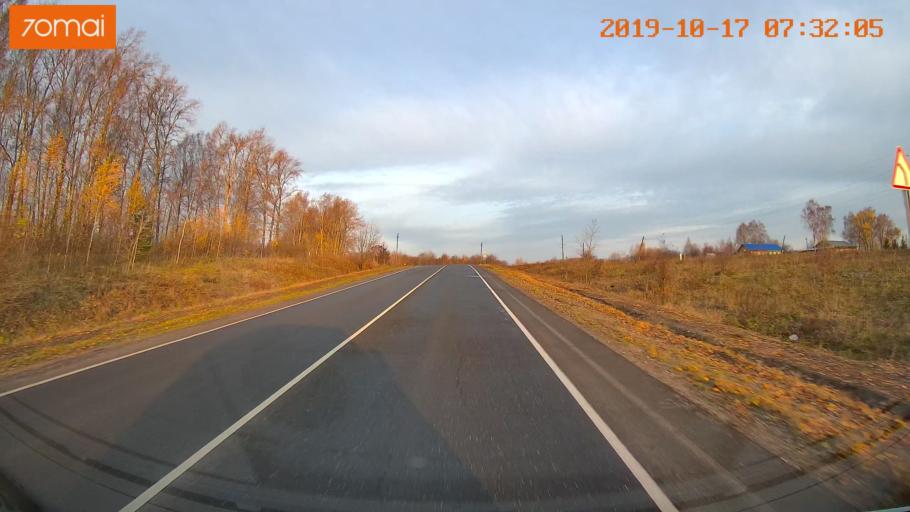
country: RU
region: Ivanovo
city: Gavrilov Posad
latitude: 56.3956
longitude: 39.9825
